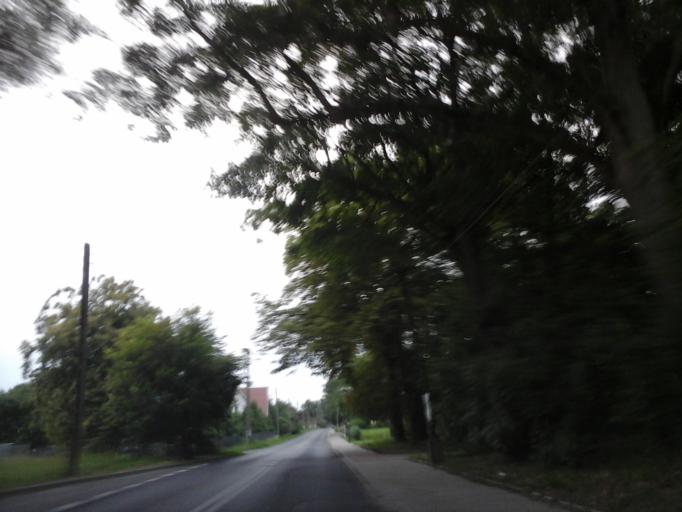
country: PL
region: West Pomeranian Voivodeship
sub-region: Powiat goleniowski
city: Nowogard
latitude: 53.5916
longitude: 15.1497
